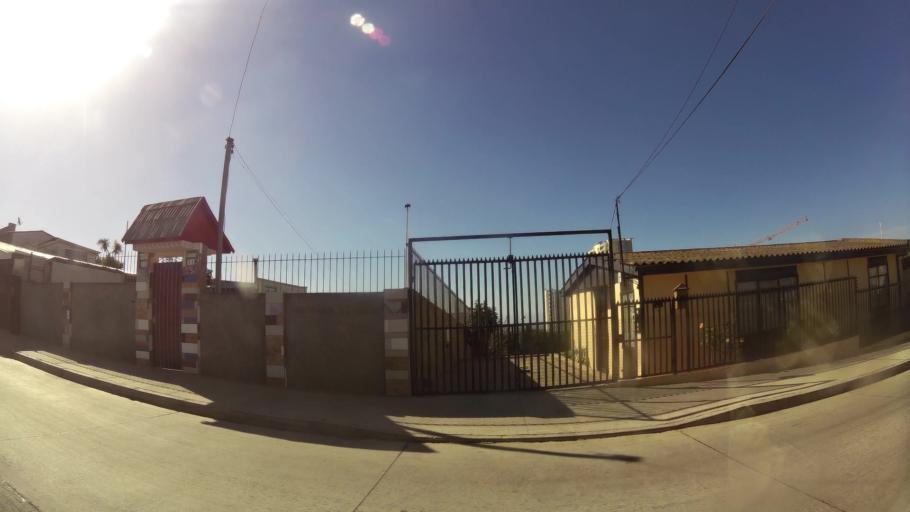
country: CL
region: Valparaiso
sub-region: Provincia de Valparaiso
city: Vina del Mar
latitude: -33.0434
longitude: -71.5565
